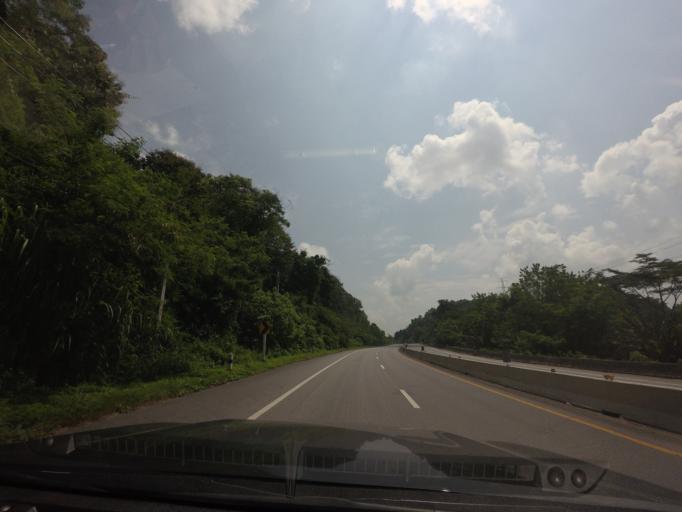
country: TH
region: Uttaradit
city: Lap Lae
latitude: 17.7800
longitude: 100.1213
